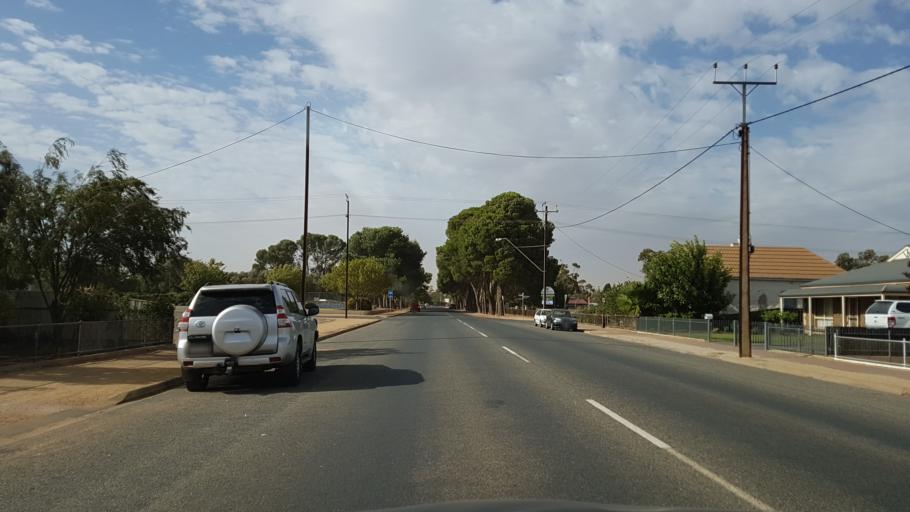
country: AU
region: South Australia
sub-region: Wakefield
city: Balaklava
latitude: -34.1483
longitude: 138.4160
